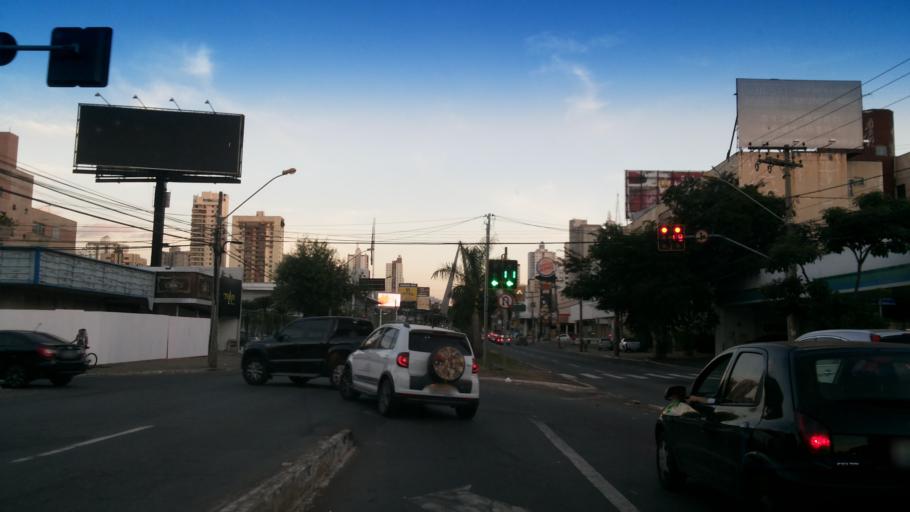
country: BR
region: Goias
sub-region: Goiania
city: Goiania
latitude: -16.7083
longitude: -49.2639
